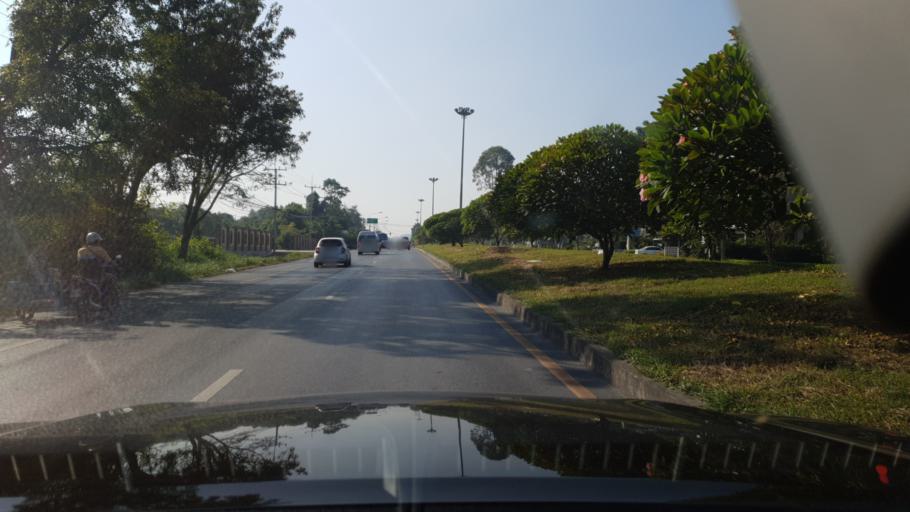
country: TH
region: Chon Buri
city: Phatthaya
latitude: 12.8045
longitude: 100.9173
